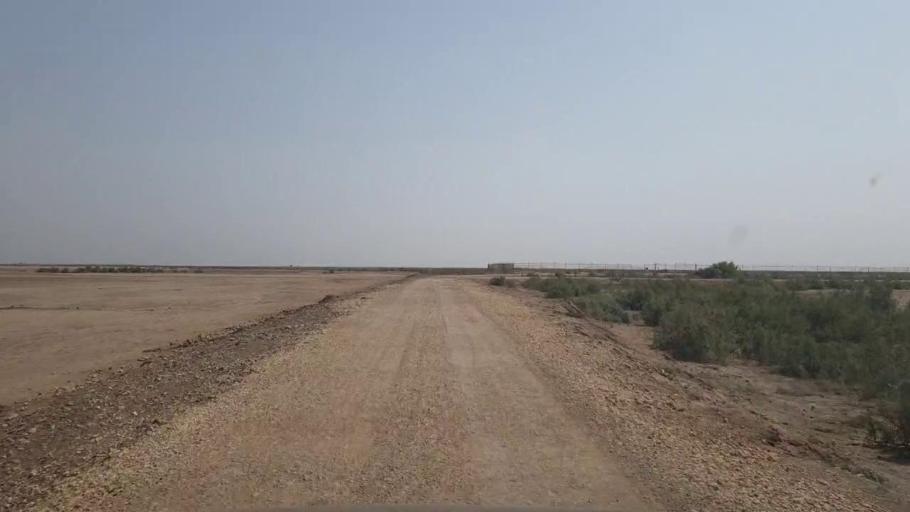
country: PK
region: Sindh
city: Jati
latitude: 24.3872
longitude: 68.5975
